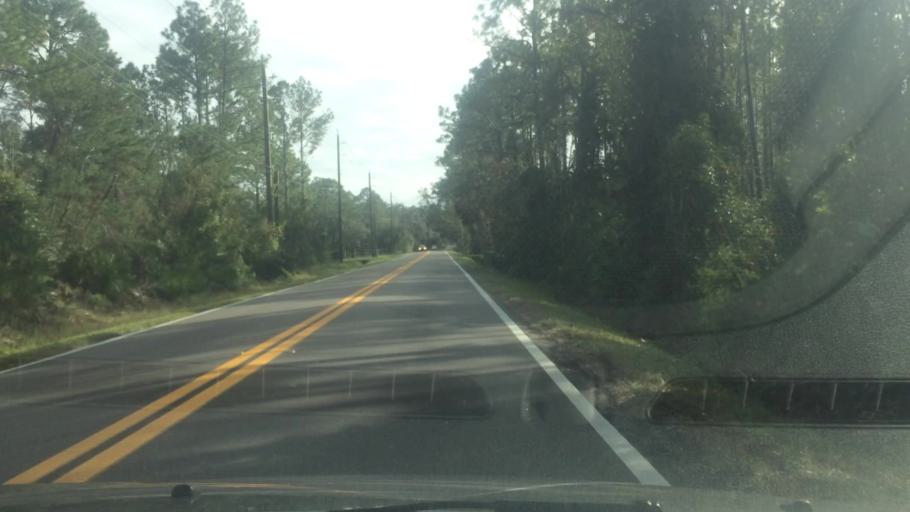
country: US
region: Florida
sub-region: Saint Johns County
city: Saint Augustine
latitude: 29.9239
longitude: -81.3613
